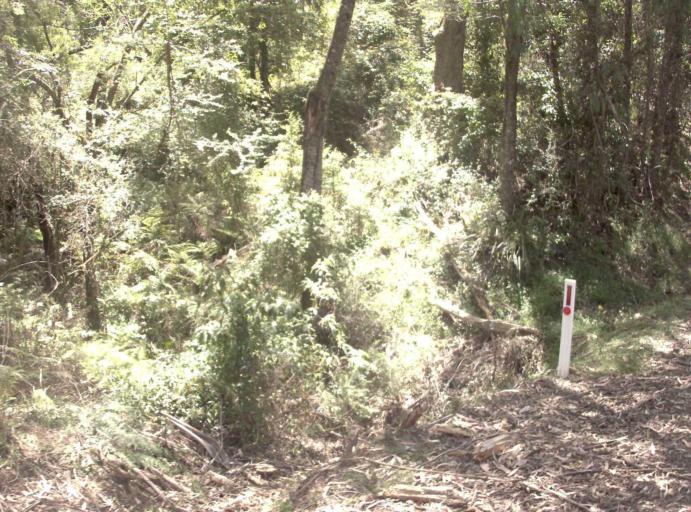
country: AU
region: New South Wales
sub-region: Bombala
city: Bombala
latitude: -37.4683
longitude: 148.9326
